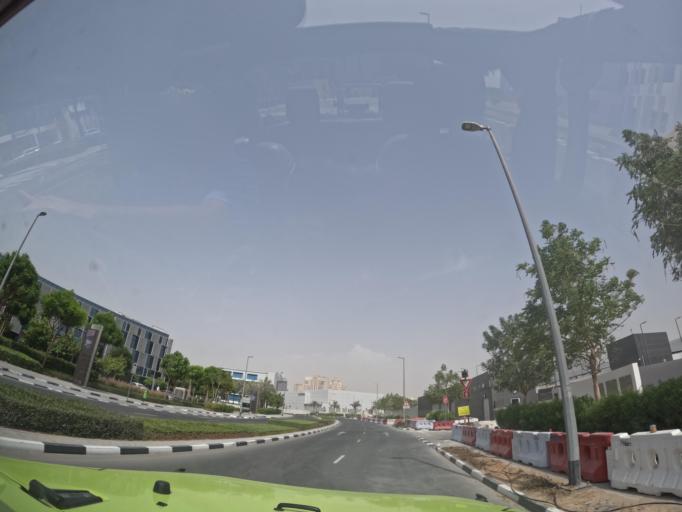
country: AE
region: Dubai
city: Dubai
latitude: 25.1183
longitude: 55.3801
